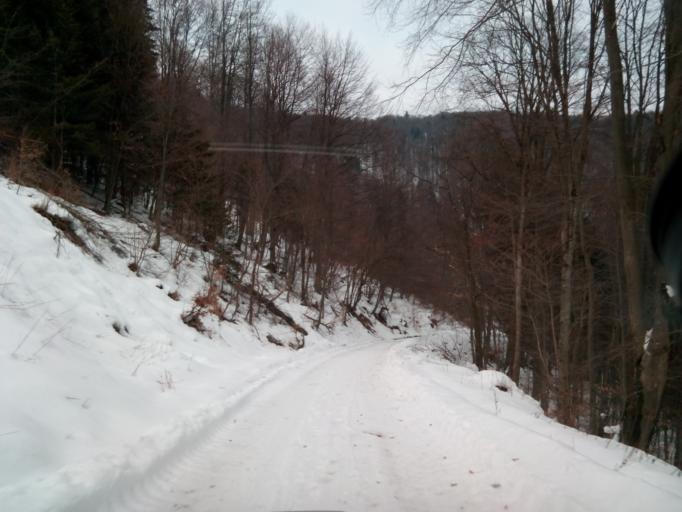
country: SK
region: Presovsky
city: Sabinov
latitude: 49.2126
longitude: 21.0914
